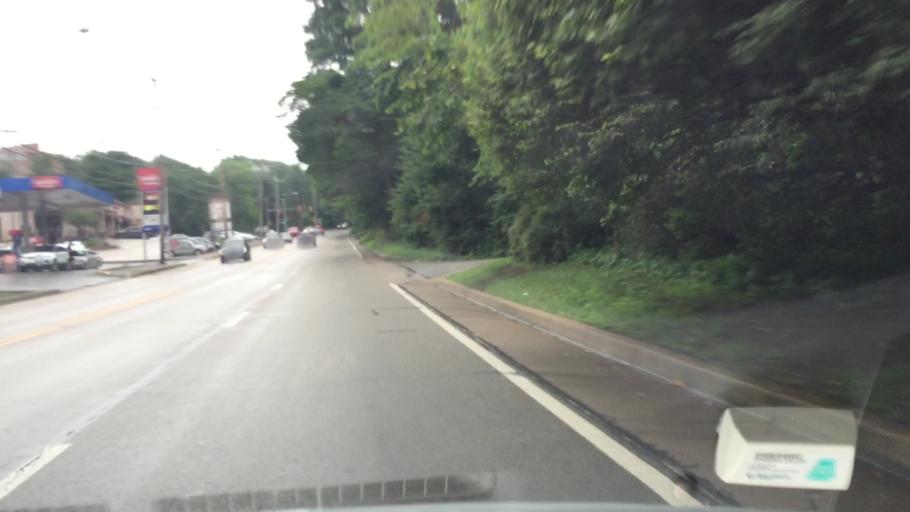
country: US
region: Pennsylvania
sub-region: Allegheny County
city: Green Tree
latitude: 40.3920
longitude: -80.0613
